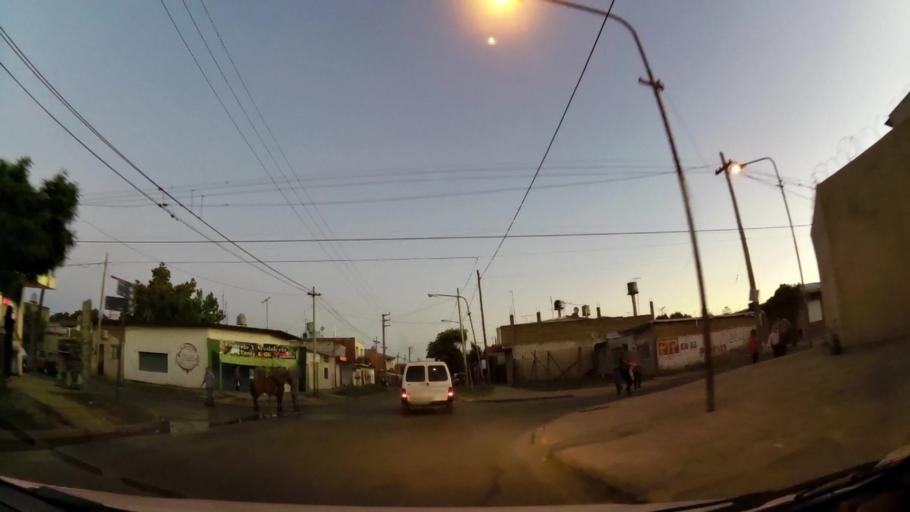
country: AR
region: Buenos Aires
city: San Justo
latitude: -34.7047
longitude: -58.6042
